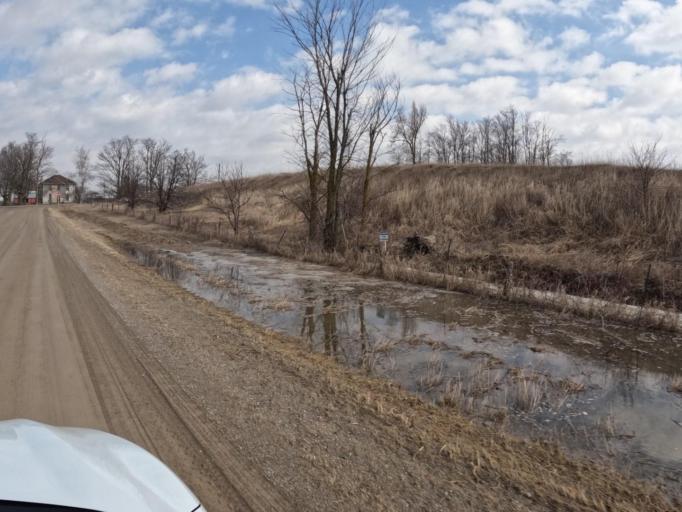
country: CA
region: Ontario
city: Shelburne
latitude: 43.9438
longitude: -80.2470
